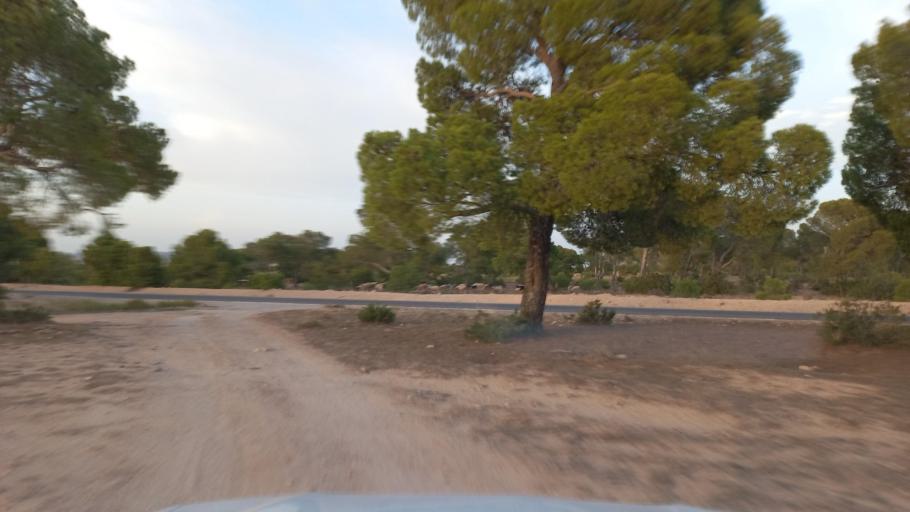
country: TN
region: Al Qasrayn
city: Sbiba
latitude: 35.4265
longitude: 8.9198
